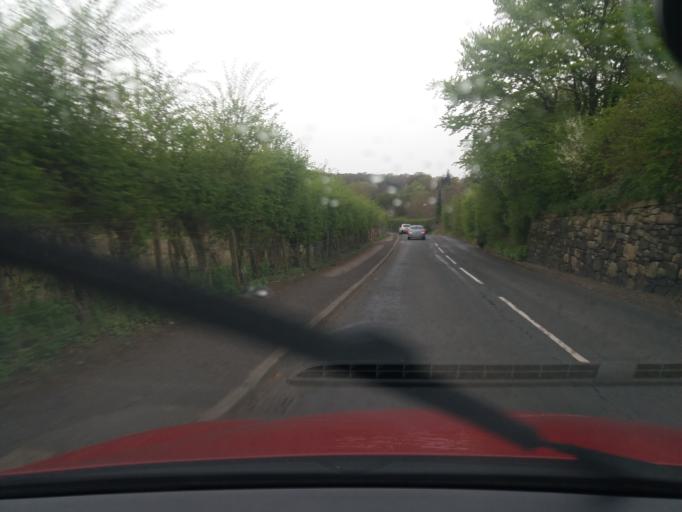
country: GB
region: England
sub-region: Lancashire
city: Chorley
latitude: 53.6841
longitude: -2.6312
